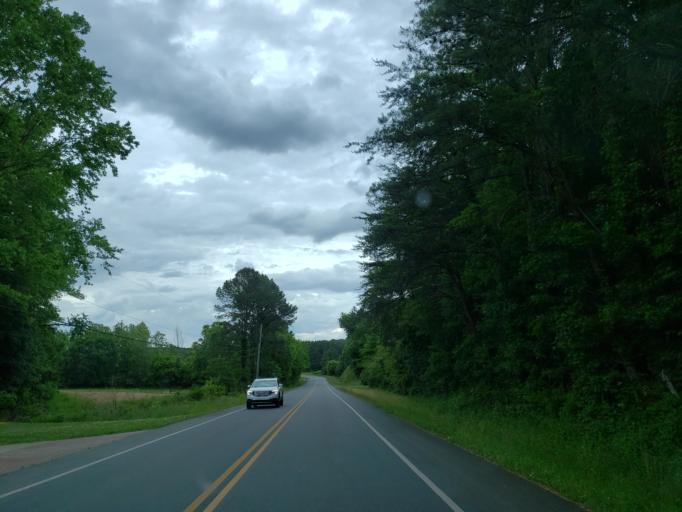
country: US
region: Georgia
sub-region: Polk County
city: Rockmart
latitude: 33.9778
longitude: -85.0441
